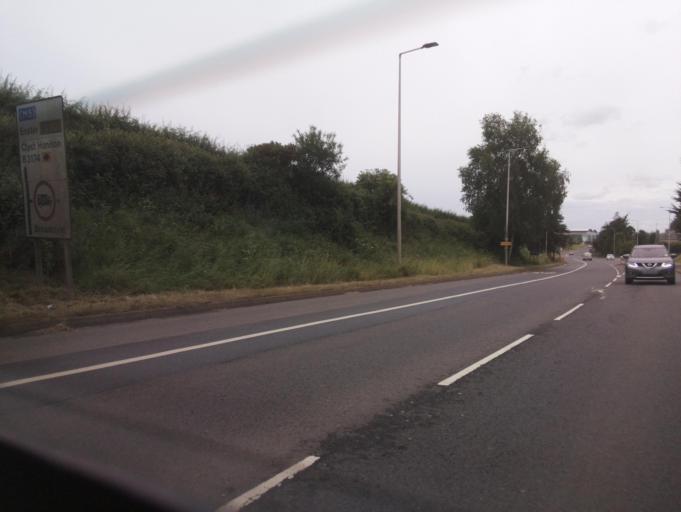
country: GB
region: England
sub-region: Devon
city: Topsham
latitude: 50.7429
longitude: -3.4196
